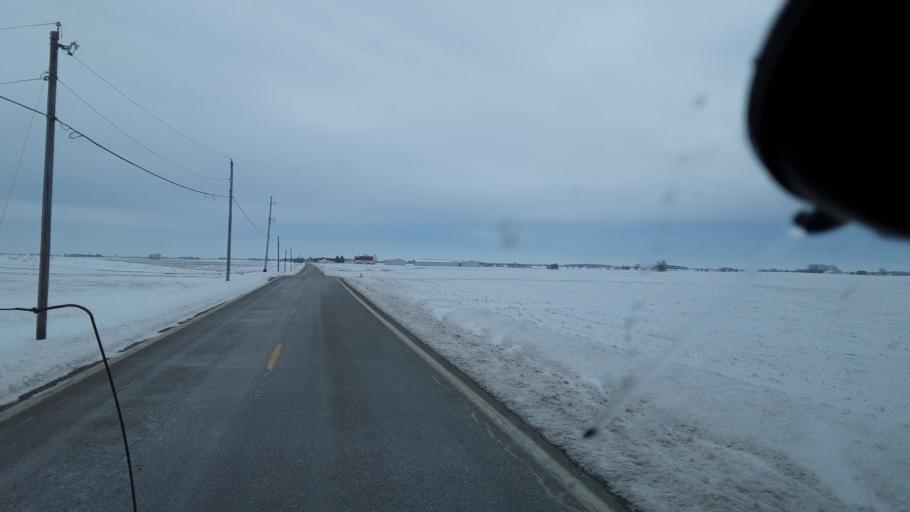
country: US
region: Ohio
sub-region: Madison County
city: Bethel
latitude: 39.7327
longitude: -83.4581
